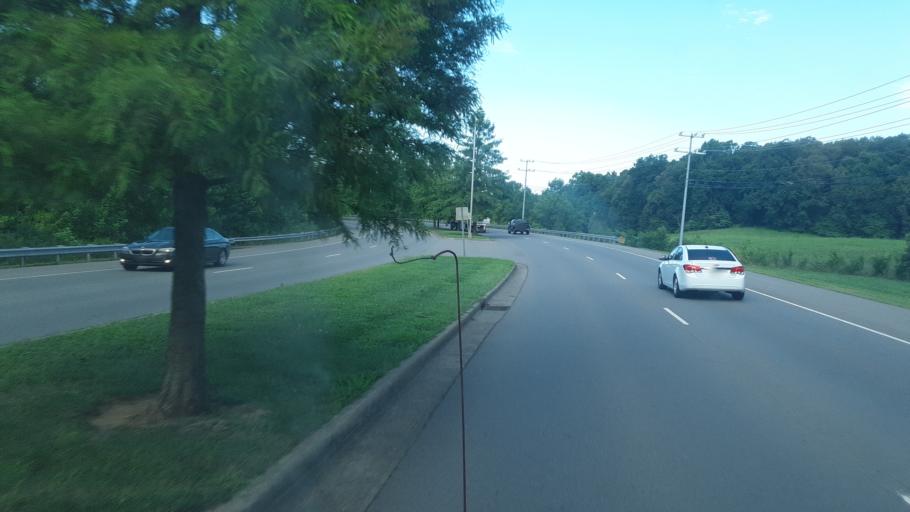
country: US
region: Tennessee
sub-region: Montgomery County
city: Clarksville
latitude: 36.5765
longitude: -87.2821
